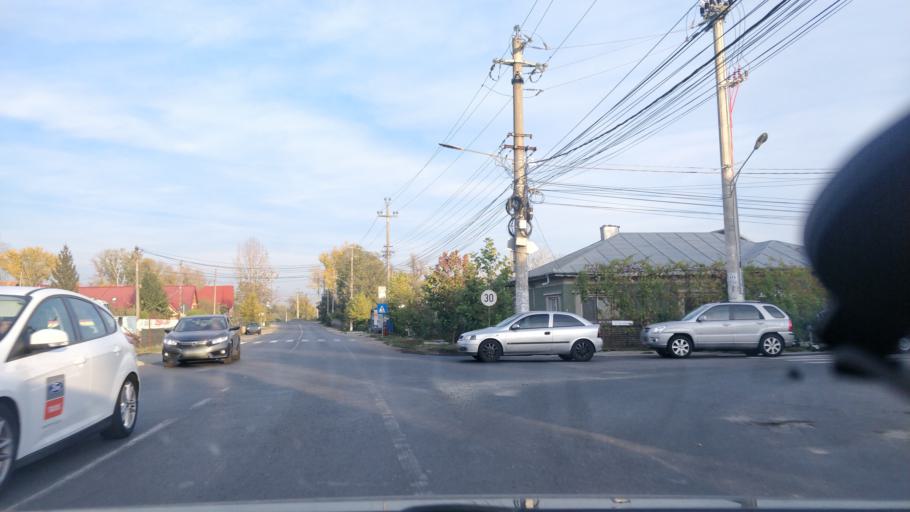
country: RO
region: Ilfov
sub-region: Comuna Ciorogarla
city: Ciorogarla
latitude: 44.4429
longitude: 25.8754
